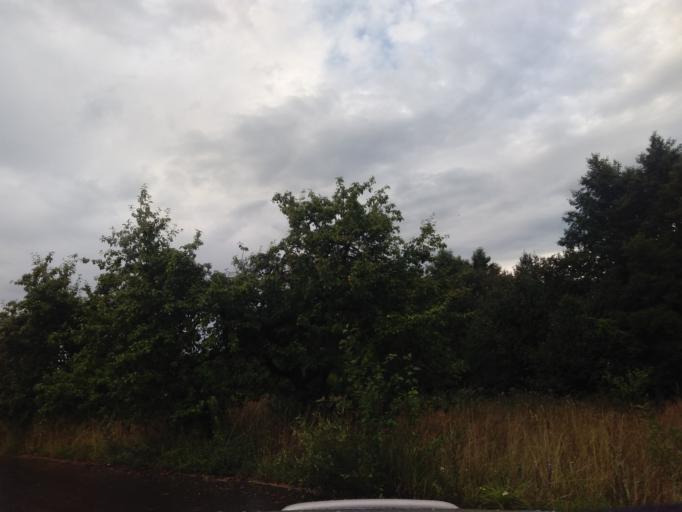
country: BY
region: Minsk
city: Kapyl'
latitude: 53.1638
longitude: 27.0929
